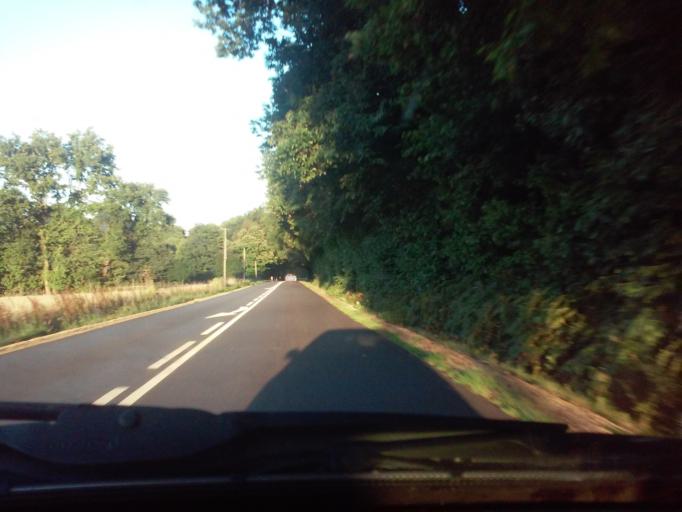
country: FR
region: Brittany
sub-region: Departement d'Ille-et-Vilaine
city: Saint-Pierre-de-Plesguen
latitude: 48.4317
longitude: -1.9242
